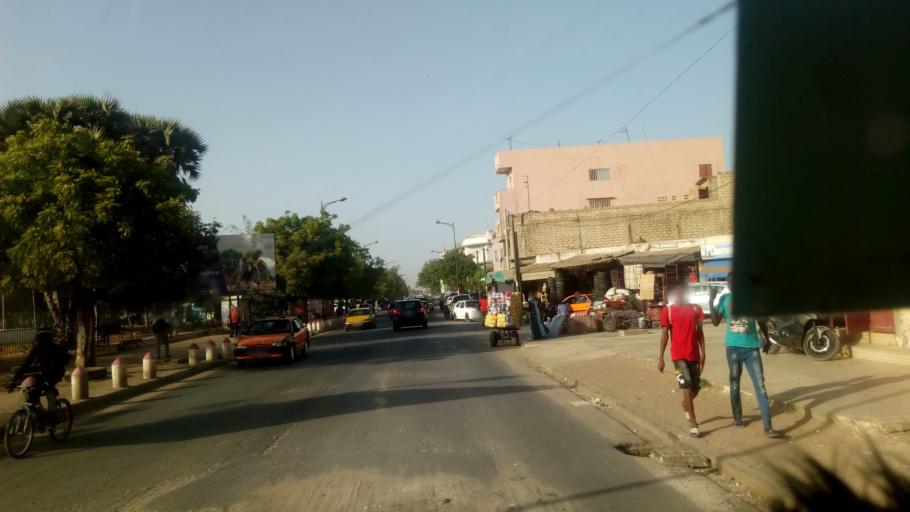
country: SN
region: Dakar
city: Dakar
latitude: 14.6947
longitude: -17.4475
